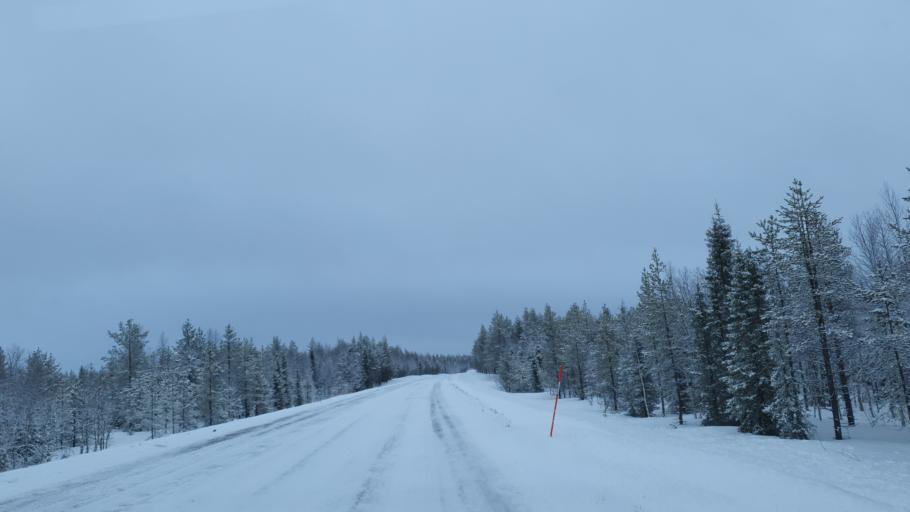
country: FI
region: Lapland
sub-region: Tunturi-Lappi
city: Kittilae
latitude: 67.5703
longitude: 24.4376
